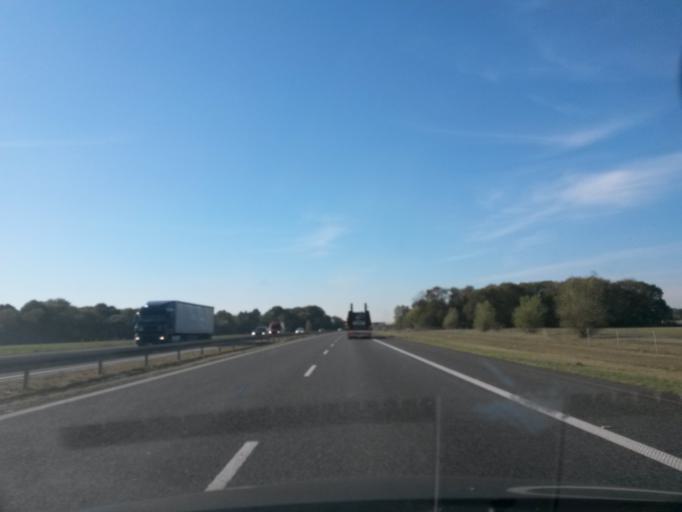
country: PL
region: Opole Voivodeship
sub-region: Powiat brzeski
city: Grodkow
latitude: 50.7726
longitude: 17.3719
